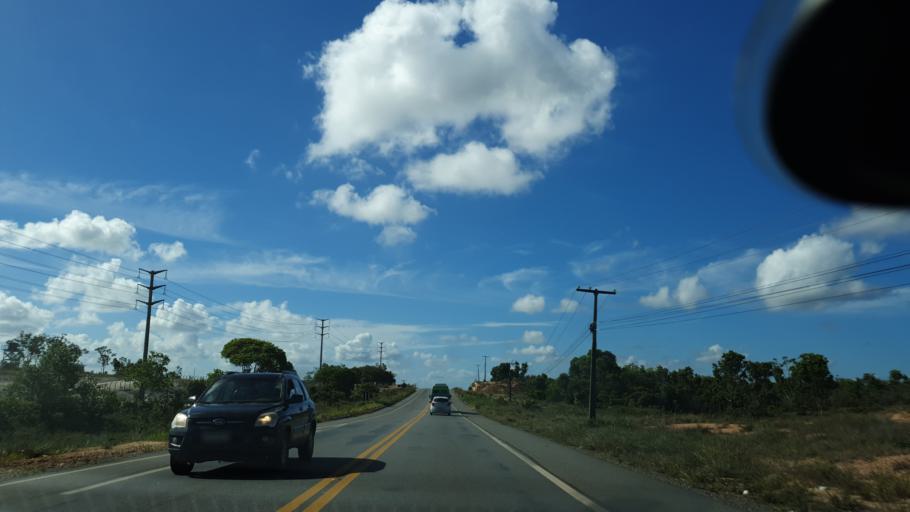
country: BR
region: Bahia
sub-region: Camacari
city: Camacari
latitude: -12.6962
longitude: -38.2210
